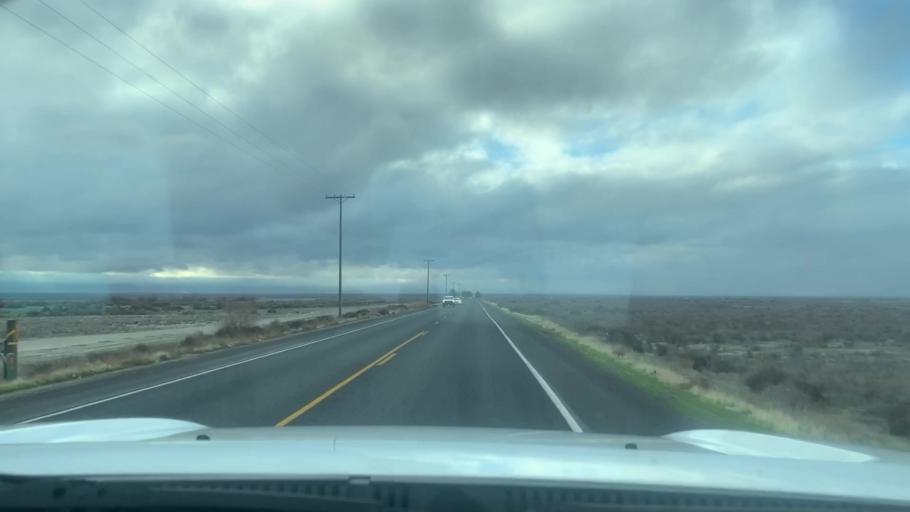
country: US
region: California
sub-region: Kern County
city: Buttonwillow
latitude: 35.4997
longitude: -119.5550
